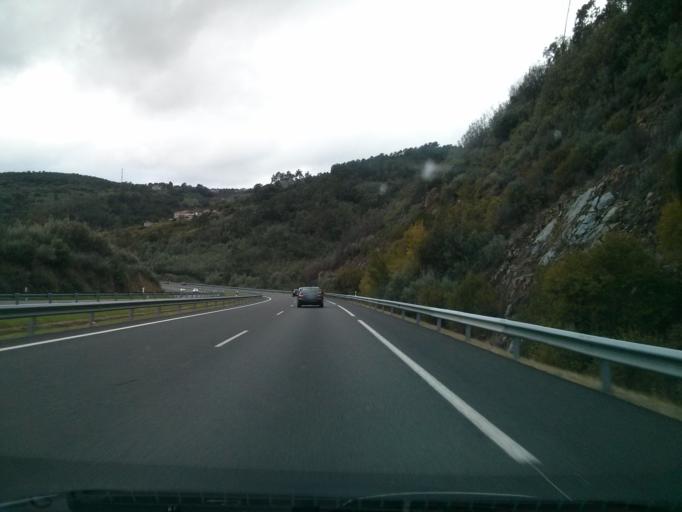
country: ES
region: Galicia
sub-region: Provincia de Ourense
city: Cenlle
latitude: 42.3346
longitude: -8.0638
